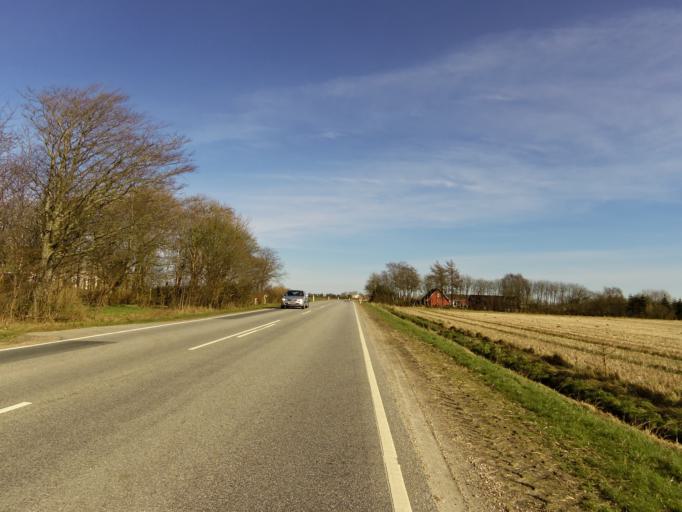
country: DK
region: South Denmark
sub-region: Vejen Kommune
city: Rodding
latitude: 55.3637
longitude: 9.0984
